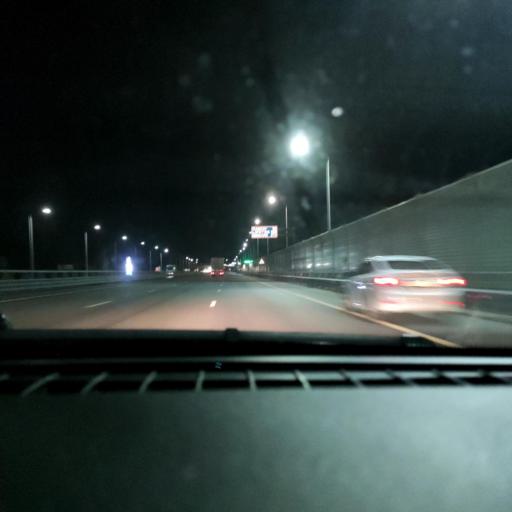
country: RU
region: Voronezj
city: Somovo
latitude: 51.6847
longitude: 39.3023
